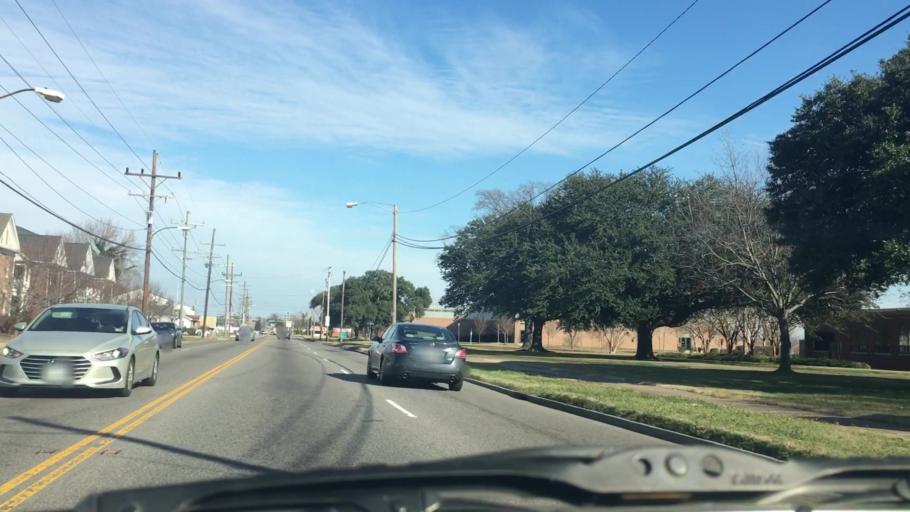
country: US
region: Virginia
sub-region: City of Norfolk
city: Norfolk
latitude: 36.8578
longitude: -76.2531
